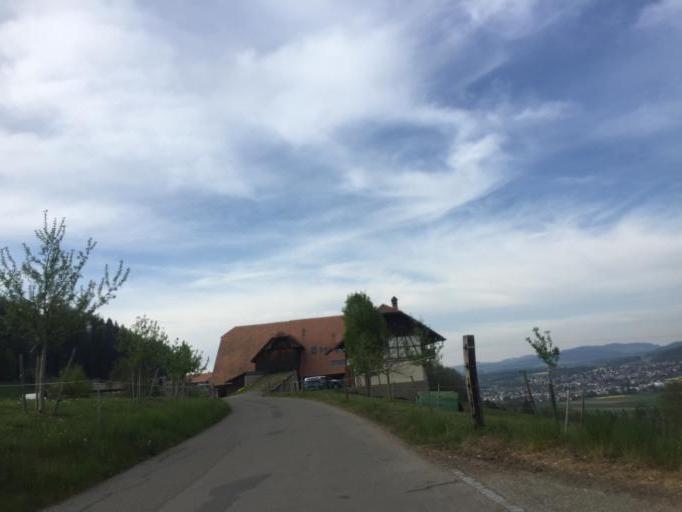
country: CH
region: Bern
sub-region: Bern-Mittelland District
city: Munsingen
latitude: 46.8493
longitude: 7.5509
